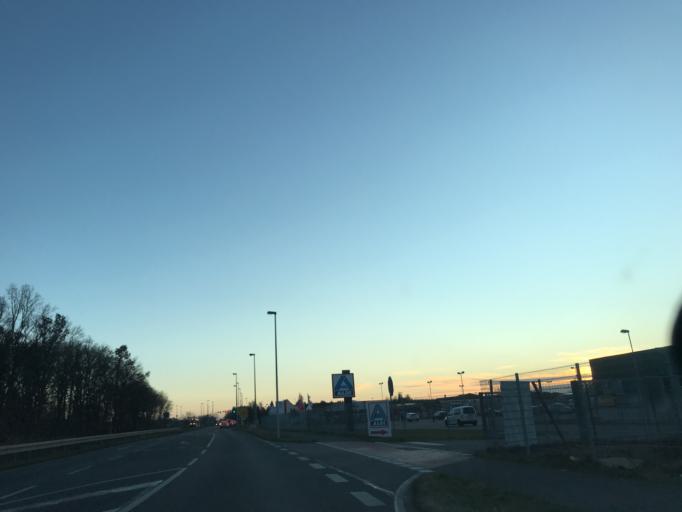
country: DE
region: Brandenburg
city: Rathenow
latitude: 52.5841
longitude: 12.3375
